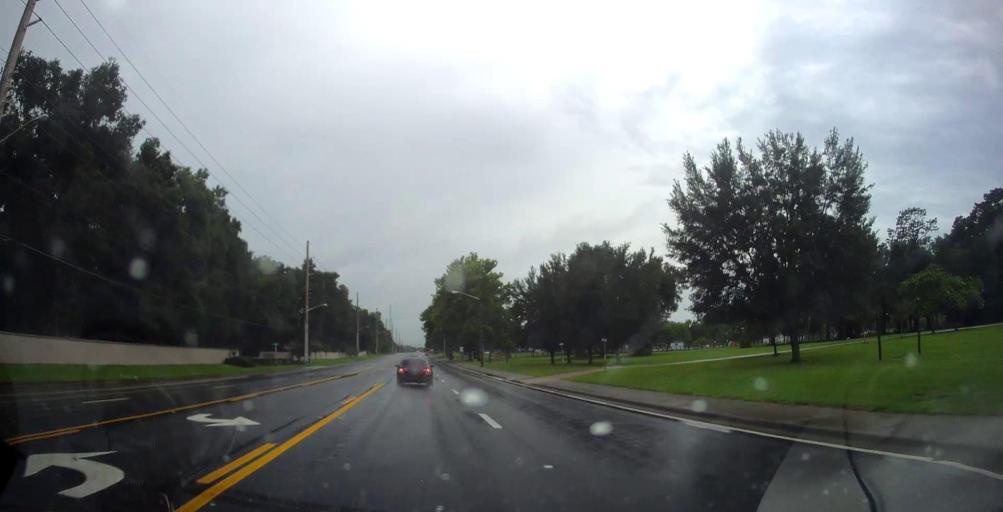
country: US
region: Florida
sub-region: Marion County
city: Ocala
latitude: 29.1689
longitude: -82.0869
